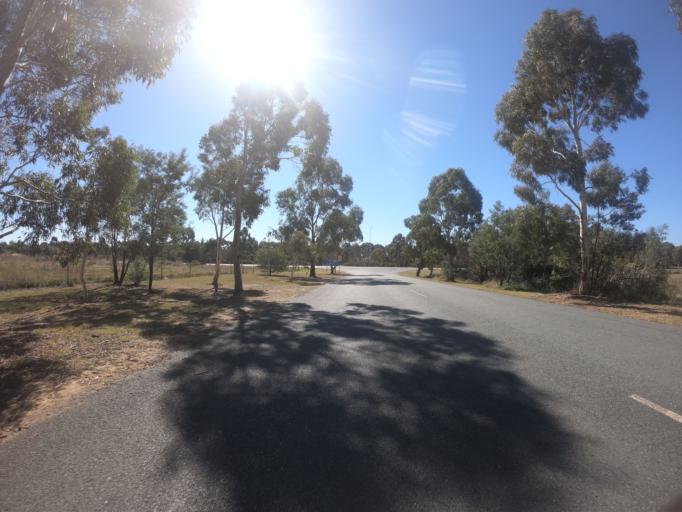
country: AU
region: Australian Capital Territory
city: Kaleen
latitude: -35.2426
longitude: 149.1042
